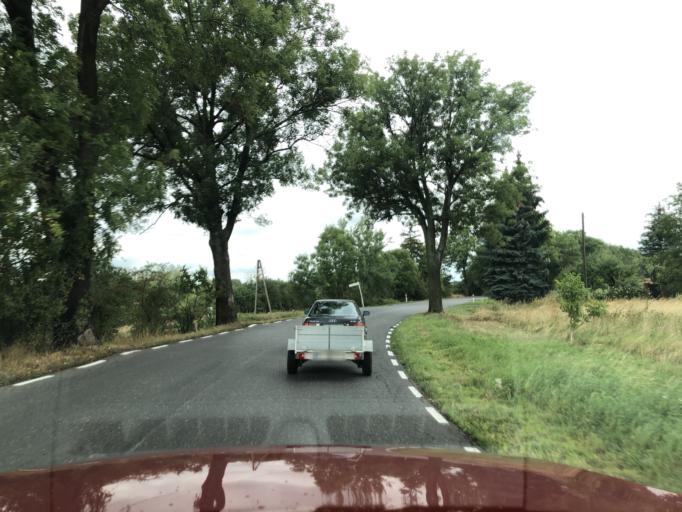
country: PL
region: Greater Poland Voivodeship
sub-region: Powiat miedzychodzki
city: Chrzypsko Wielkie
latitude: 52.5928
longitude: 16.3008
